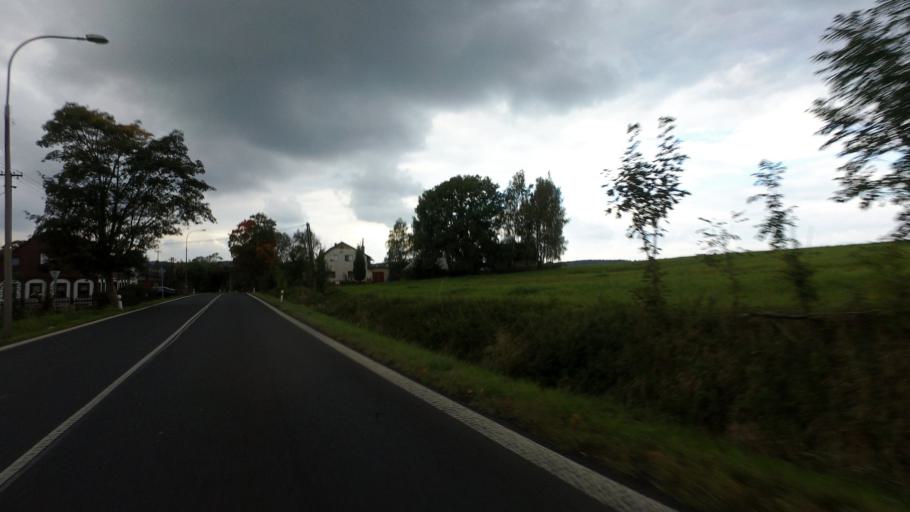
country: CZ
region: Ustecky
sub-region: Okres Decin
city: Rumburk
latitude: 50.9624
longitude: 14.5354
